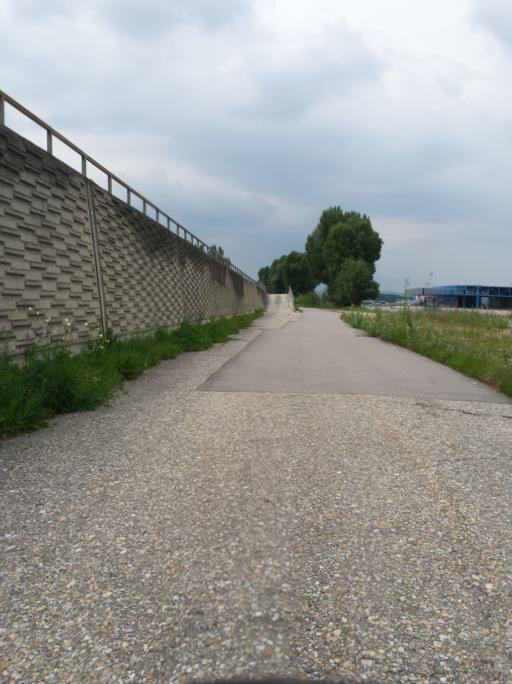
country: AT
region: Lower Austria
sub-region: Politischer Bezirk Wien-Umgebung
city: Schwechat
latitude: 48.1722
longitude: 16.4783
